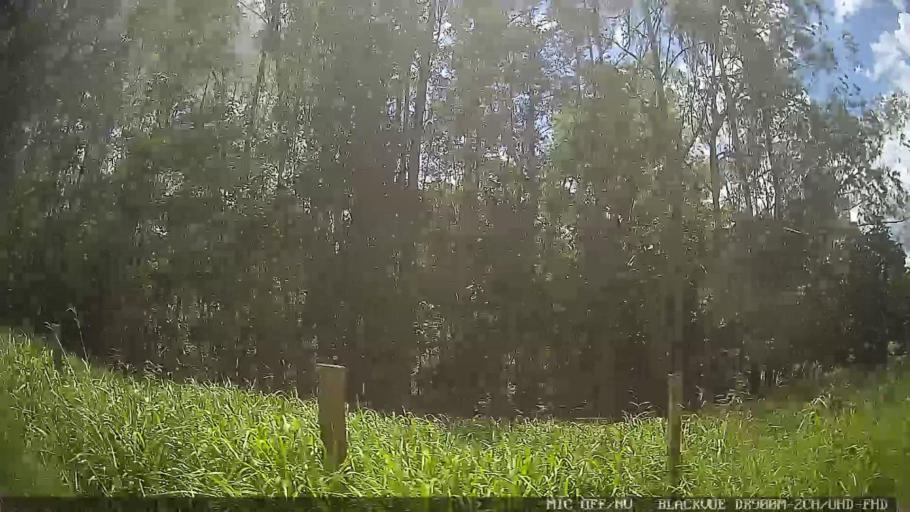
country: BR
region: Sao Paulo
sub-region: Piracaia
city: Piracaia
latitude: -23.0138
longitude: -46.4542
